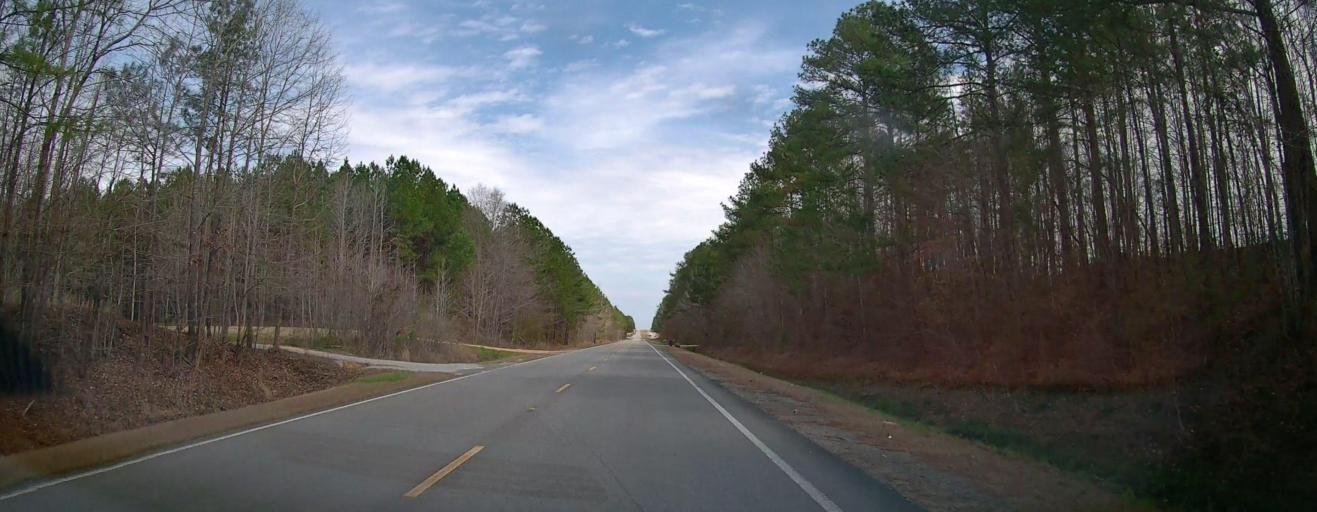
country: US
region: Alabama
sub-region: Marion County
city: Winfield
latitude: 33.9350
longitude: -87.7170
